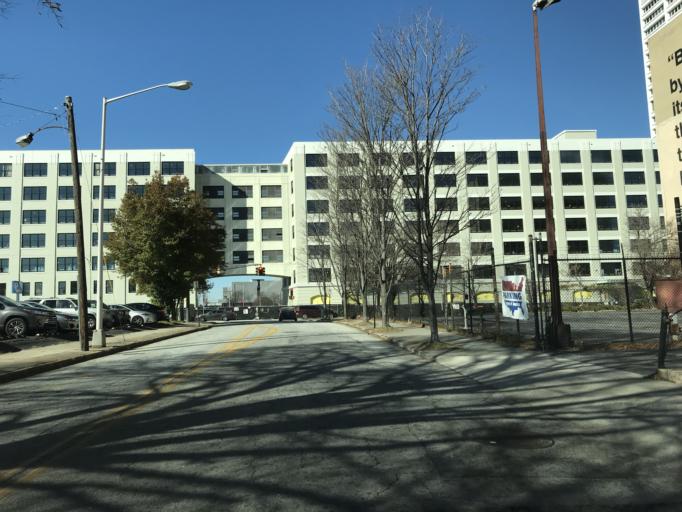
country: US
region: Georgia
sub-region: Fulton County
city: Atlanta
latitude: 33.7515
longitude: -84.3955
